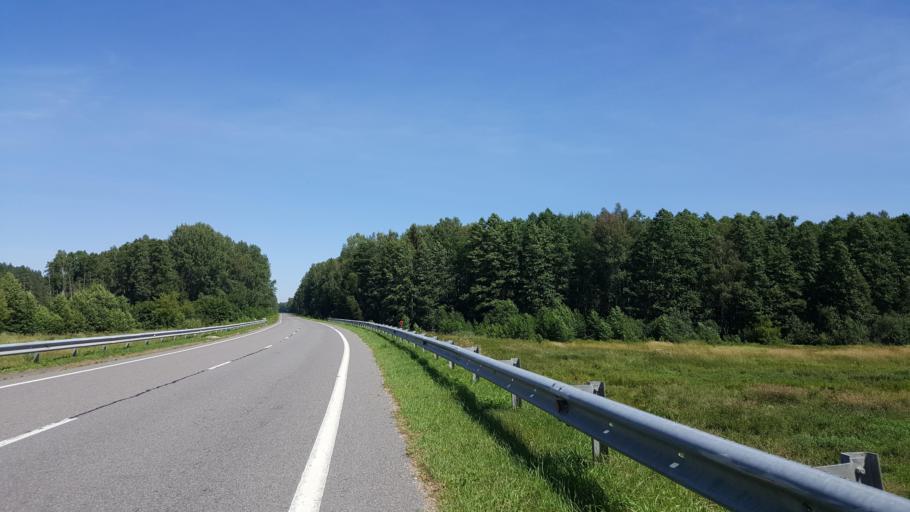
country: BY
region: Brest
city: Pruzhany
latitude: 52.5009
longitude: 24.1750
